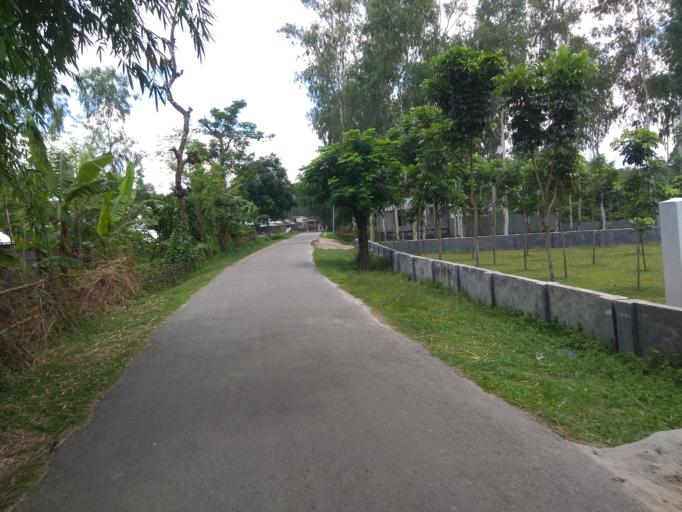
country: IN
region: West Bengal
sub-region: Koch Bihar
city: Haldibari
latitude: 26.1988
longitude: 88.9225
